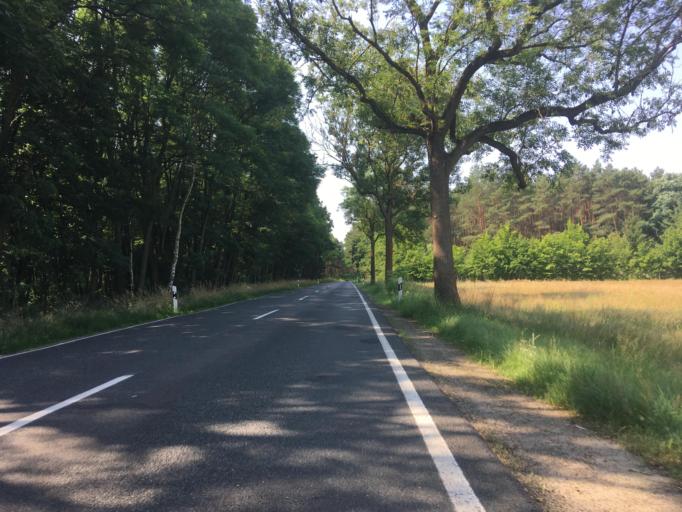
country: DE
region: Brandenburg
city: Golzow
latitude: 52.2965
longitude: 12.6784
